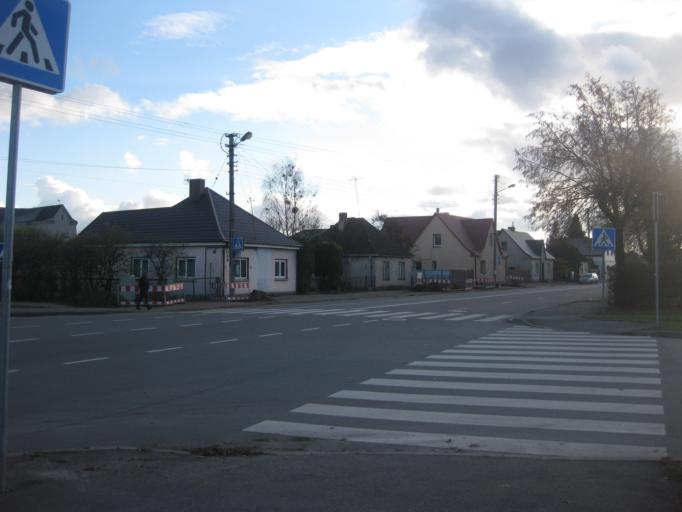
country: LT
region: Kauno apskritis
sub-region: Kaunas
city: Silainiai
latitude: 54.9195
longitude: 23.8964
